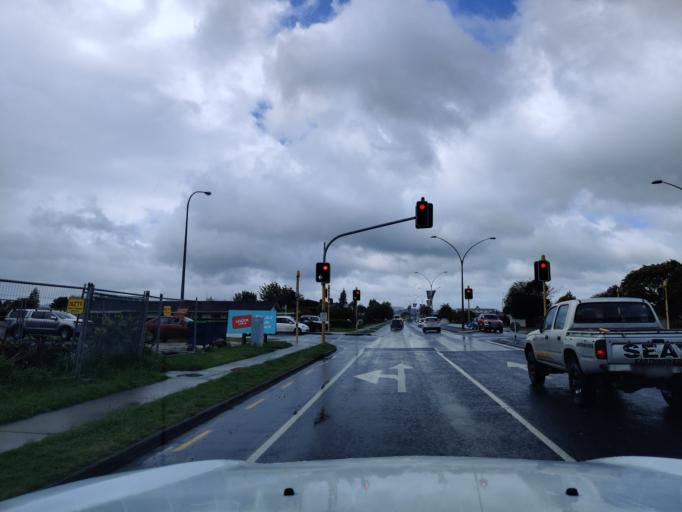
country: NZ
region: Bay of Plenty
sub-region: Rotorua District
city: Rotorua
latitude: -38.1123
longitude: 176.2246
